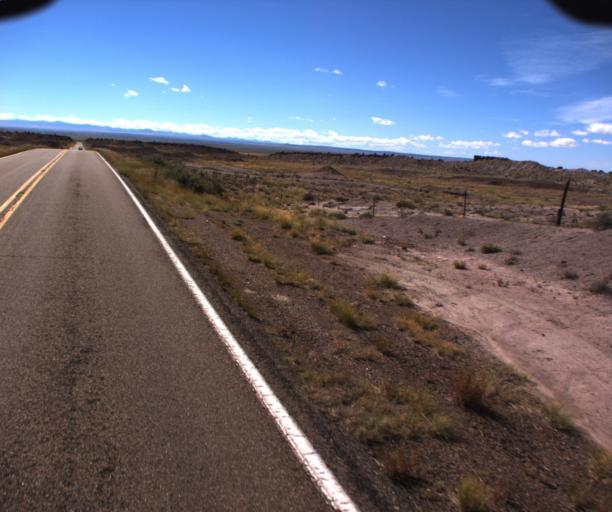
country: US
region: Arizona
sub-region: Apache County
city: Saint Johns
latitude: 34.6582
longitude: -109.2951
